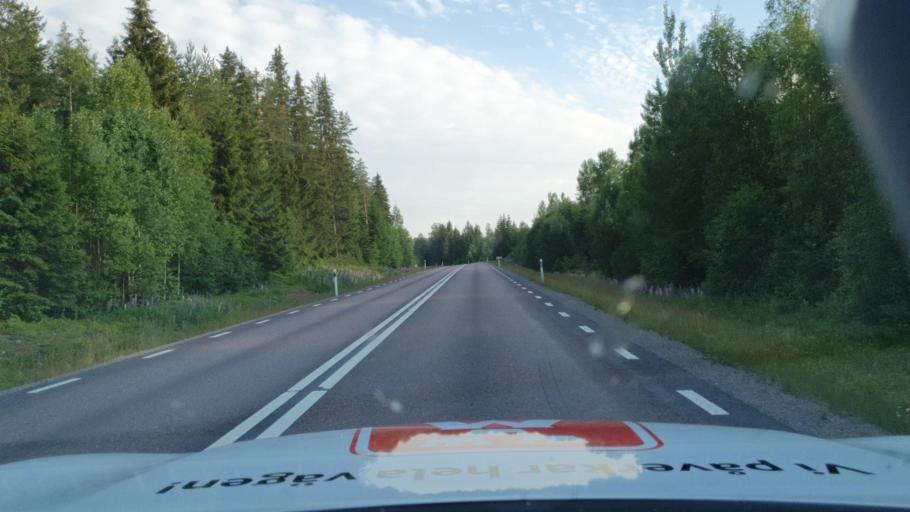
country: SE
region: Vaermland
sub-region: Hagfors Kommun
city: Hagfors
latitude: 60.0030
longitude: 13.6438
